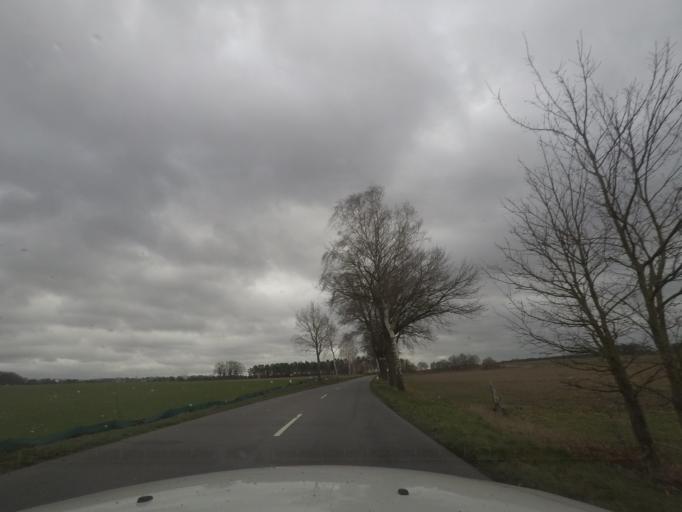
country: DE
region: Lower Saxony
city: Emmendorf
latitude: 53.0382
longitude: 10.6049
